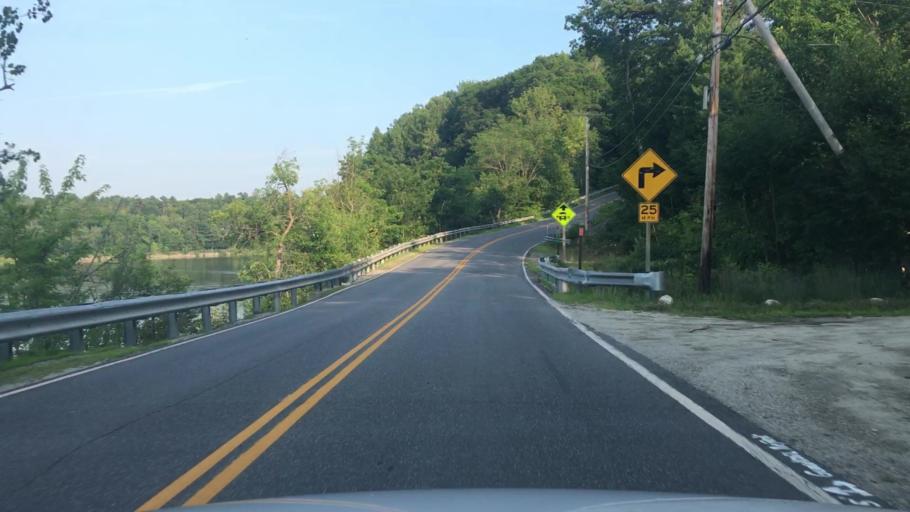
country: US
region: Maine
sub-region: Androscoggin County
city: Lisbon Falls
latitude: 43.9910
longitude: -70.0544
